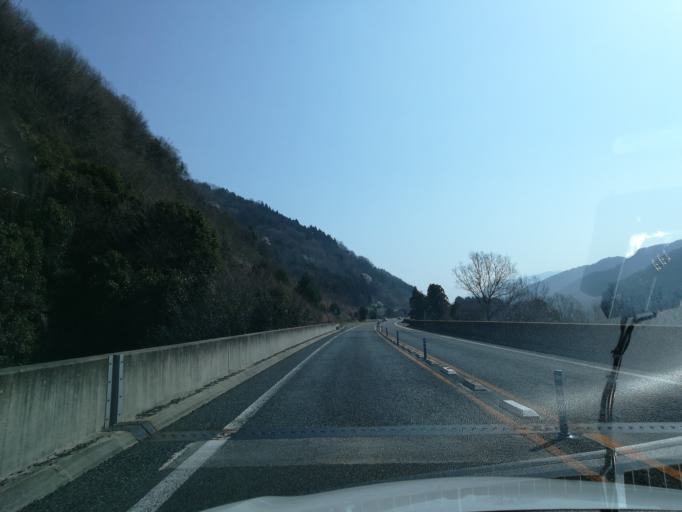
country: JP
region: Tokushima
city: Ikedacho
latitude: 34.0107
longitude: 133.7285
